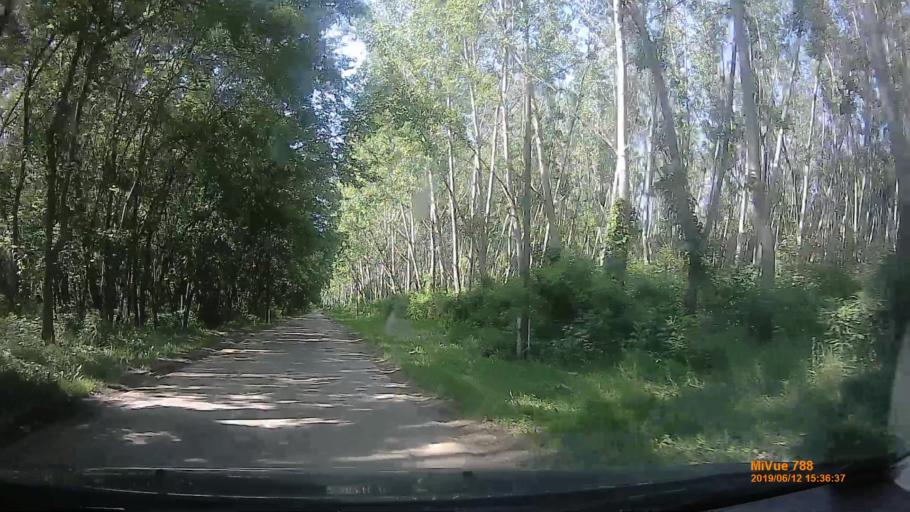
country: HU
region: Csongrad
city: Mako
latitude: 46.2007
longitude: 20.4665
